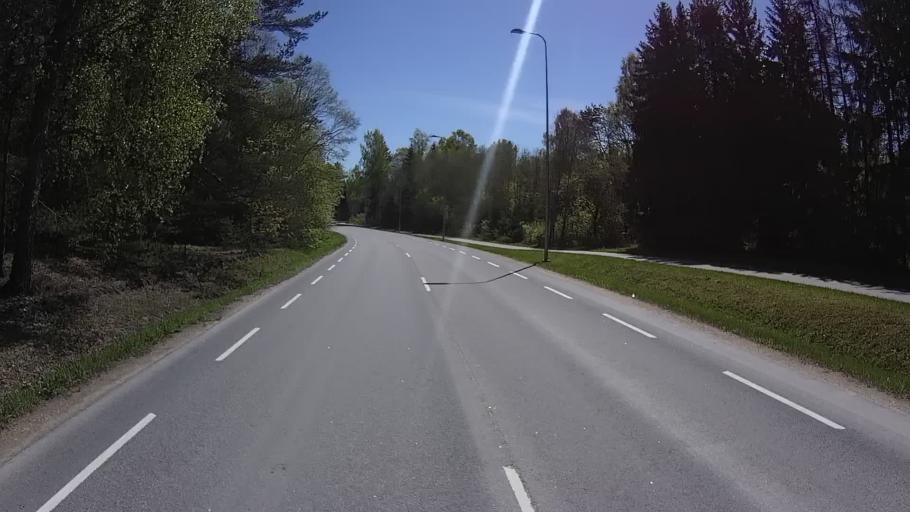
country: EE
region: Harju
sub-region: Raasiku vald
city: Raasiku
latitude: 59.1739
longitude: 25.1707
